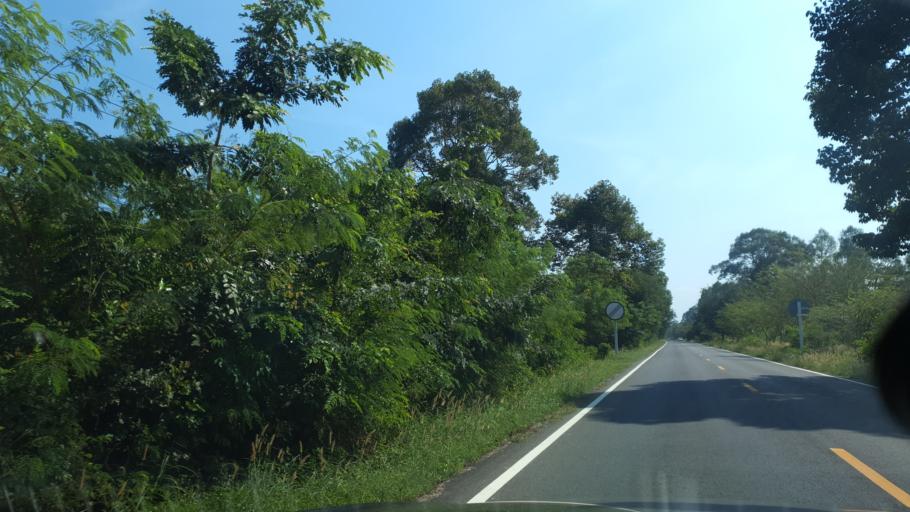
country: TH
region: Surat Thani
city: Tha Chana
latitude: 9.5825
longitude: 99.2027
